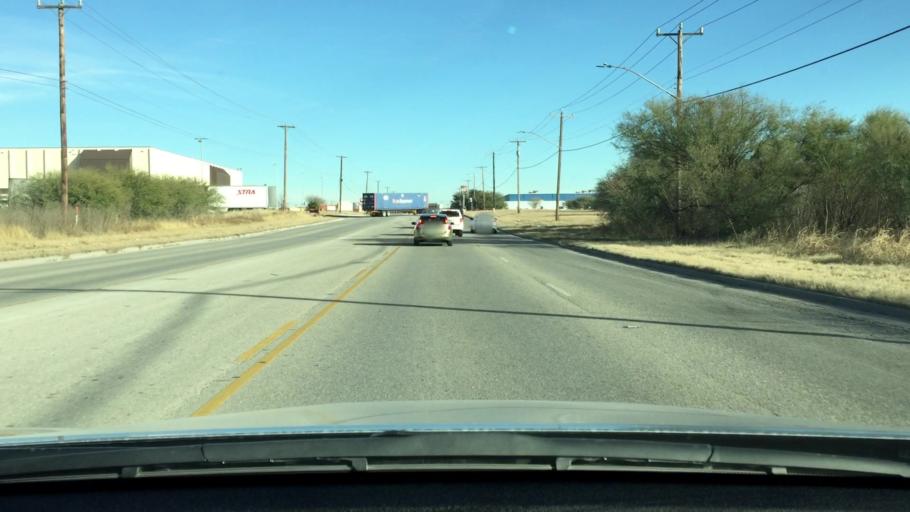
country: US
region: Texas
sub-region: Bexar County
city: Kirby
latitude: 29.4822
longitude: -98.3677
